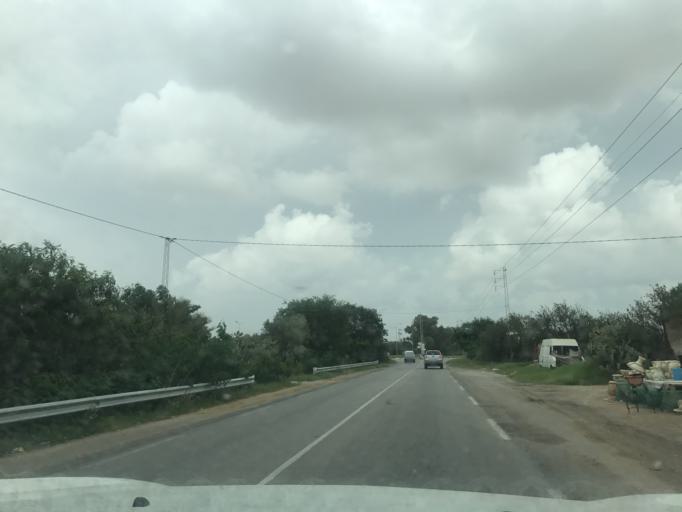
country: TN
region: Al Munastir
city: Qasr Hallal
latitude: 35.6011
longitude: 10.8997
